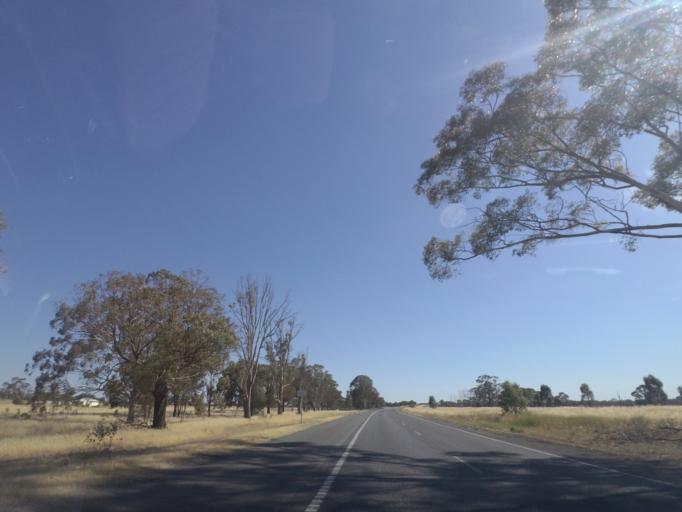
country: AU
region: Victoria
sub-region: Greater Shepparton
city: Shepparton
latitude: -36.6062
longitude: 145.3226
